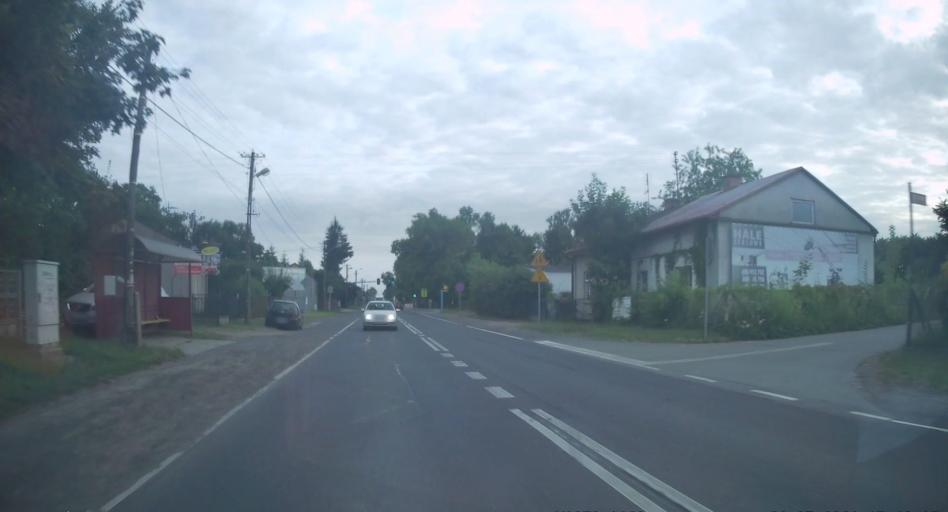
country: PL
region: Lodz Voivodeship
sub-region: Powiat radomszczanski
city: Radomsko
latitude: 51.0977
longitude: 19.4605
